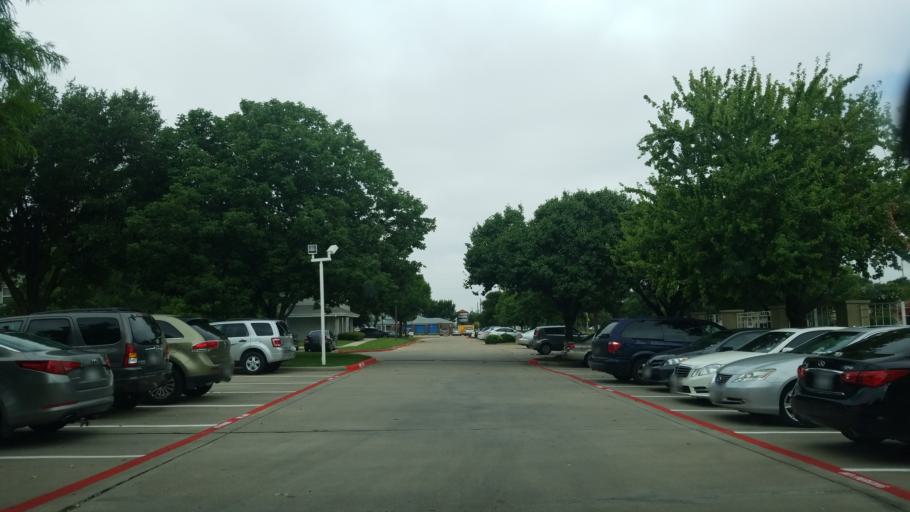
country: US
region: Texas
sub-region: Dallas County
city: Farmers Branch
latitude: 32.9094
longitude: -96.8657
